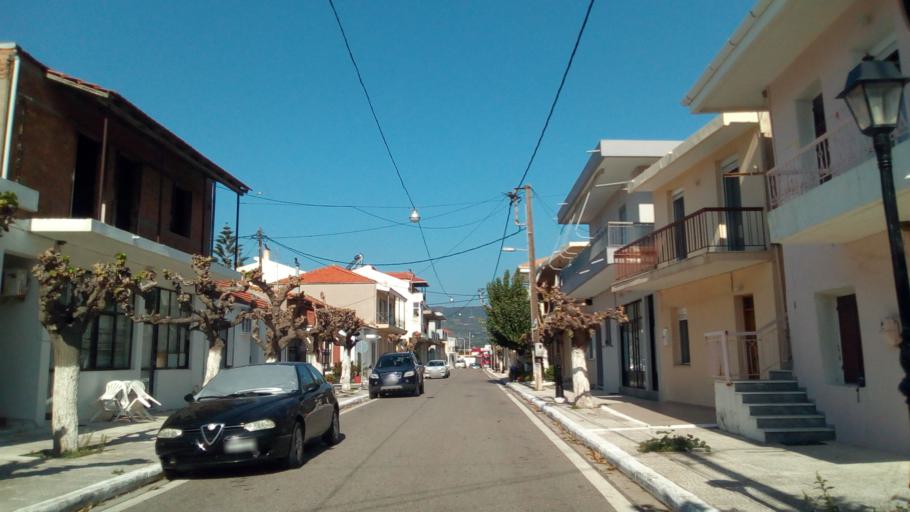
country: GR
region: West Greece
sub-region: Nomos Aitolias kai Akarnanias
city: Antirrio
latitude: 38.3305
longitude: 21.7642
